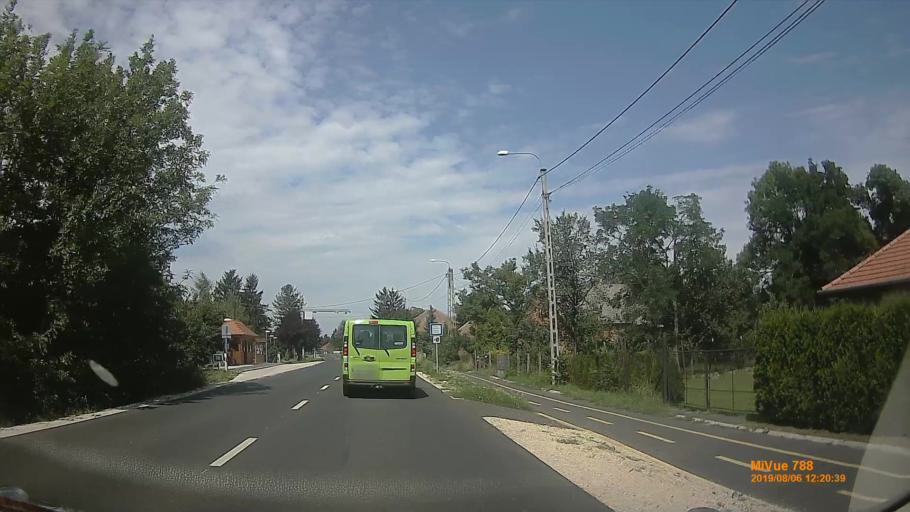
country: HU
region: Vas
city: Taplanszentkereszt
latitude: 47.1812
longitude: 16.7485
